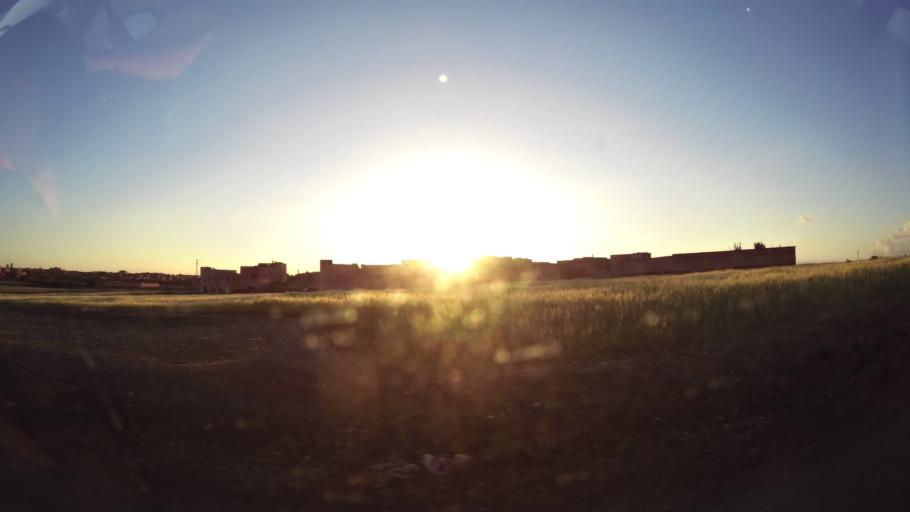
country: MA
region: Marrakech-Tensift-Al Haouz
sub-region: Kelaa-Des-Sraghna
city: Sidi Abdallah
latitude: 32.2372
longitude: -7.9283
